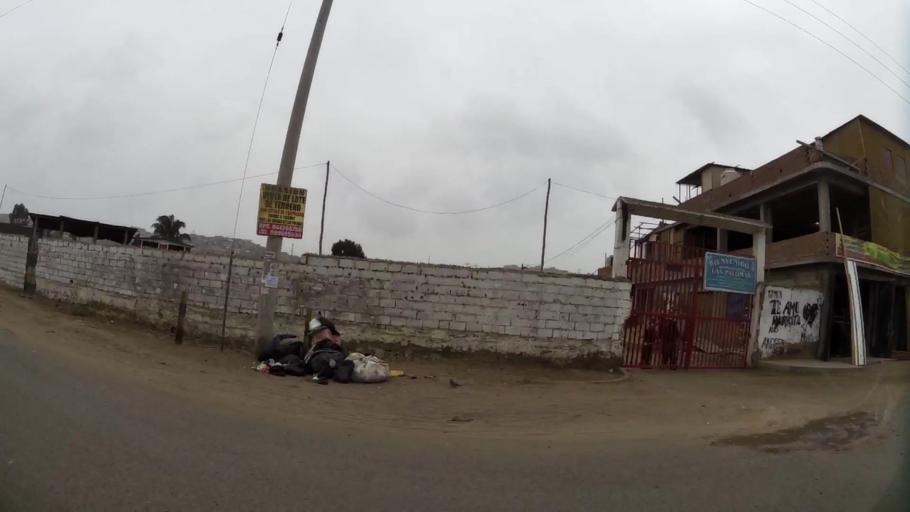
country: PE
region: Lima
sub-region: Lima
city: Cieneguilla
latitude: -12.2264
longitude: -76.9025
